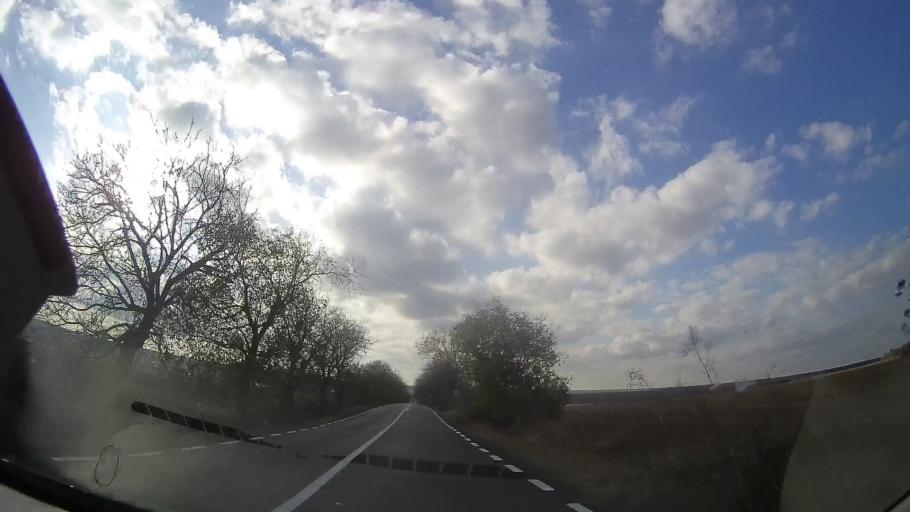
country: RO
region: Constanta
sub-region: Comuna Albesti
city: Albesti
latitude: 43.8138
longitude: 28.4473
